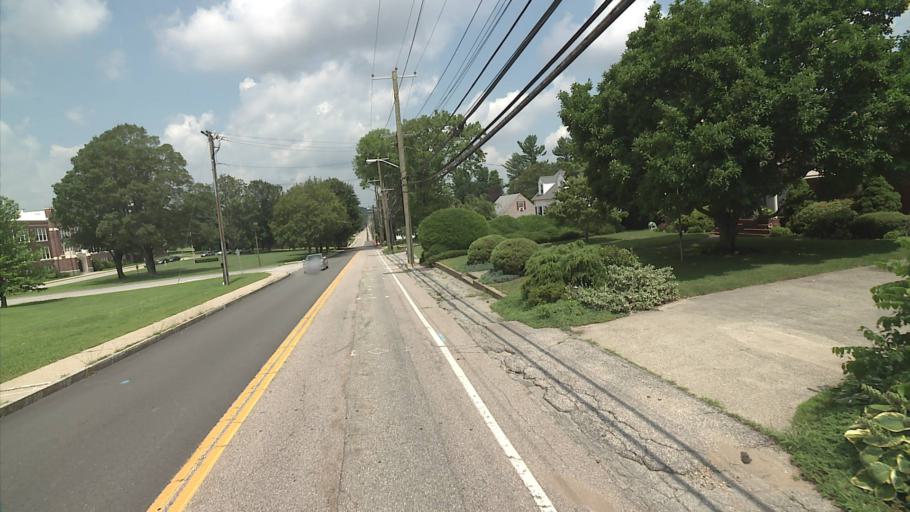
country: US
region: Connecticut
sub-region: New London County
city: Jewett City
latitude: 41.5970
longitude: -71.9784
